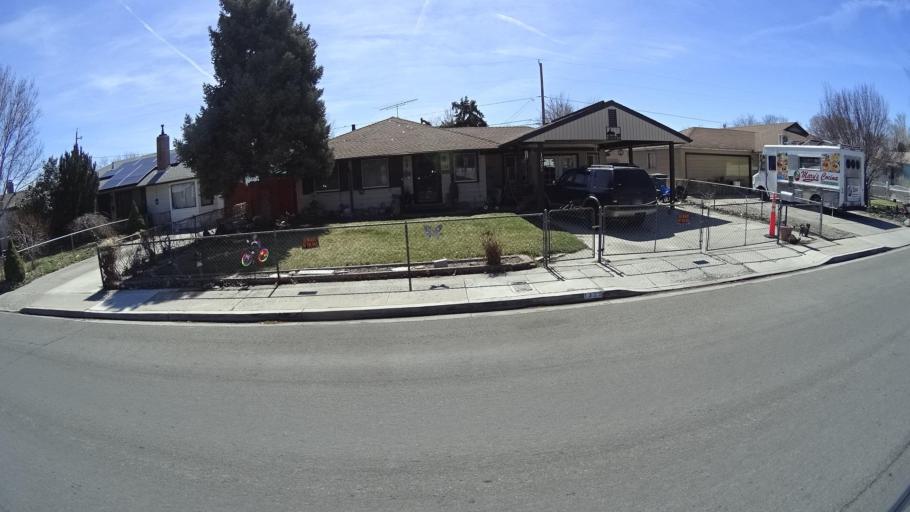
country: US
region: Nevada
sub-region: Washoe County
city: Sparks
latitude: 39.5474
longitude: -119.7603
